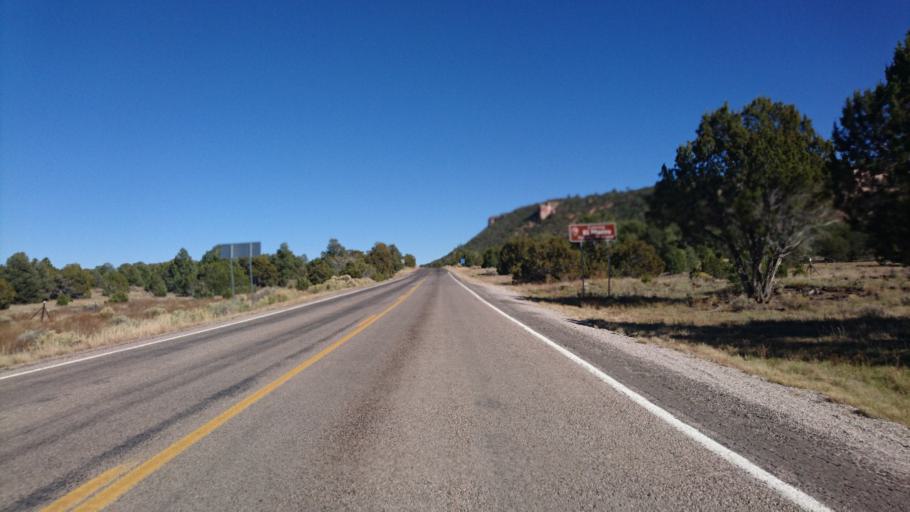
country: US
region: New Mexico
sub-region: McKinley County
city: Thoreau
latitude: 35.0435
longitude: -108.3293
